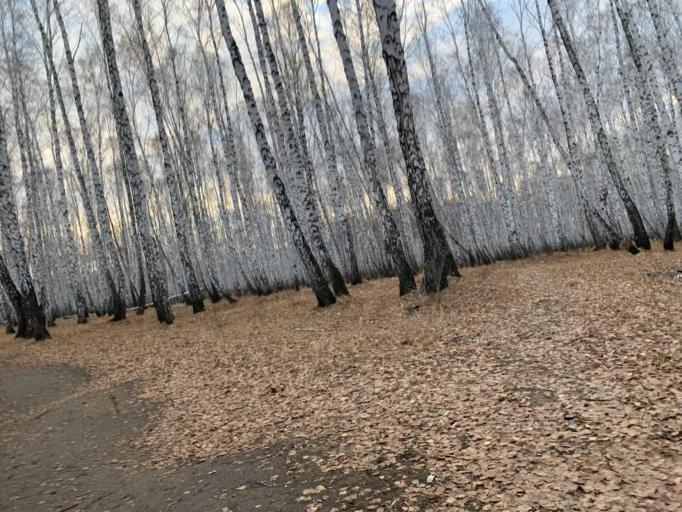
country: RU
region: Chelyabinsk
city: Roshchino
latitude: 55.2050
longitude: 61.3119
